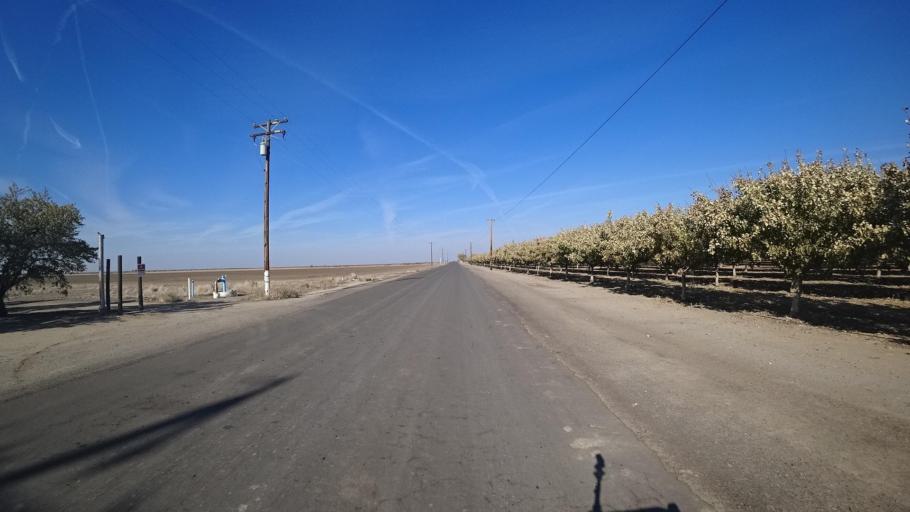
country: US
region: California
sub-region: Kern County
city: Wasco
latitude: 35.6777
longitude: -119.3840
